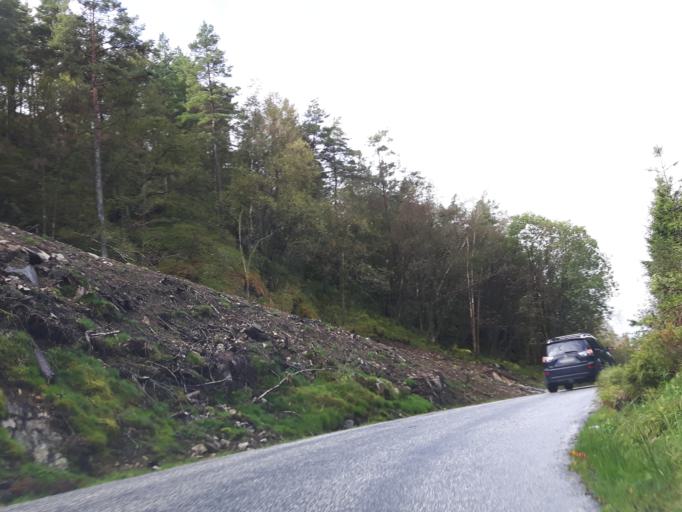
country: NO
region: Rogaland
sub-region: Lund
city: Moi
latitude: 58.3957
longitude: 6.6296
